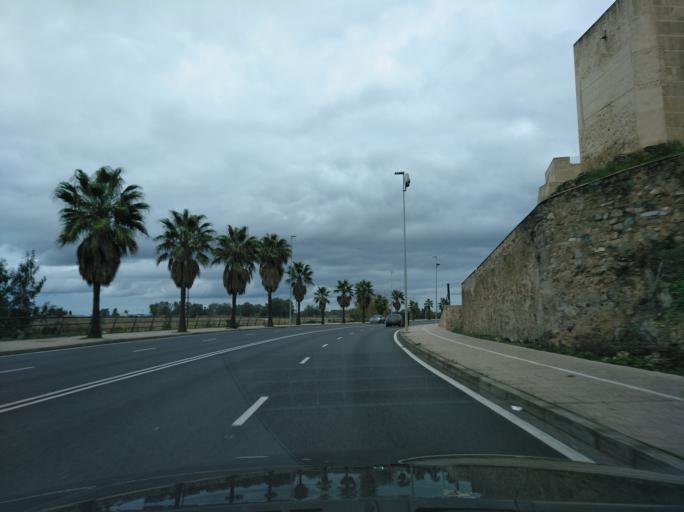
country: ES
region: Extremadura
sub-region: Provincia de Badajoz
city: Badajoz
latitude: 38.8846
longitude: -6.9697
